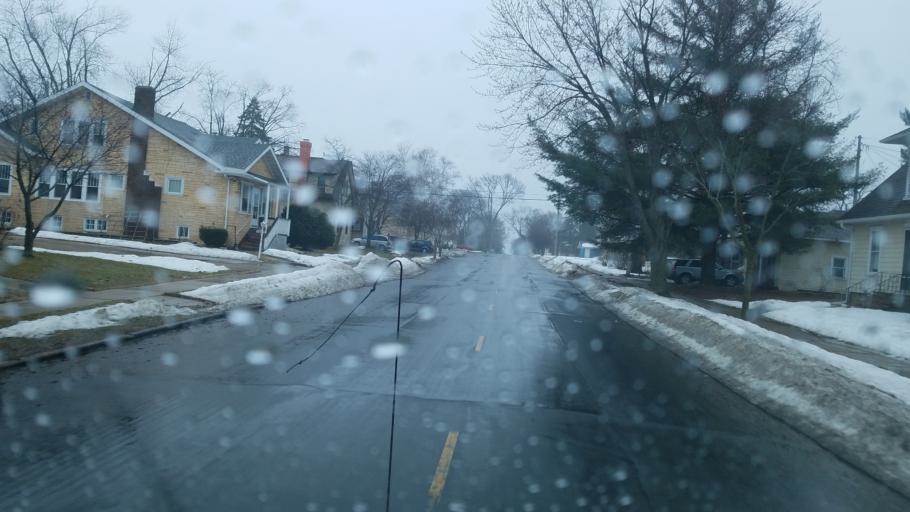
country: US
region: Wisconsin
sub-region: Wood County
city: Marshfield
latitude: 44.6639
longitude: -90.1721
